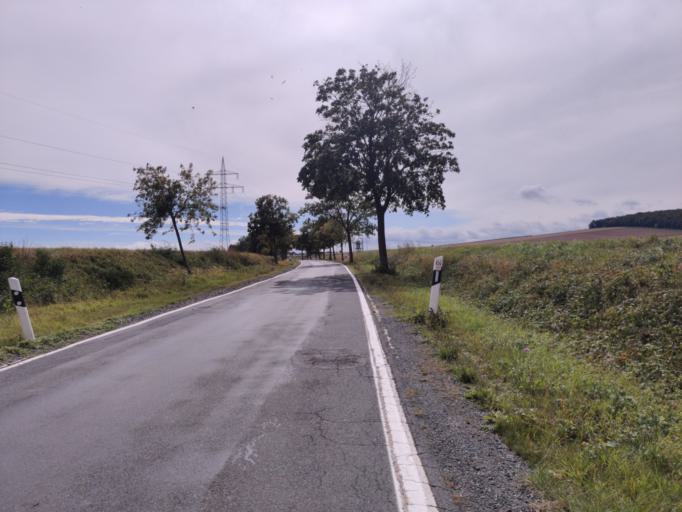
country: DE
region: Lower Saxony
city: Alt Wallmoden
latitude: 52.0182
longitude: 10.3316
